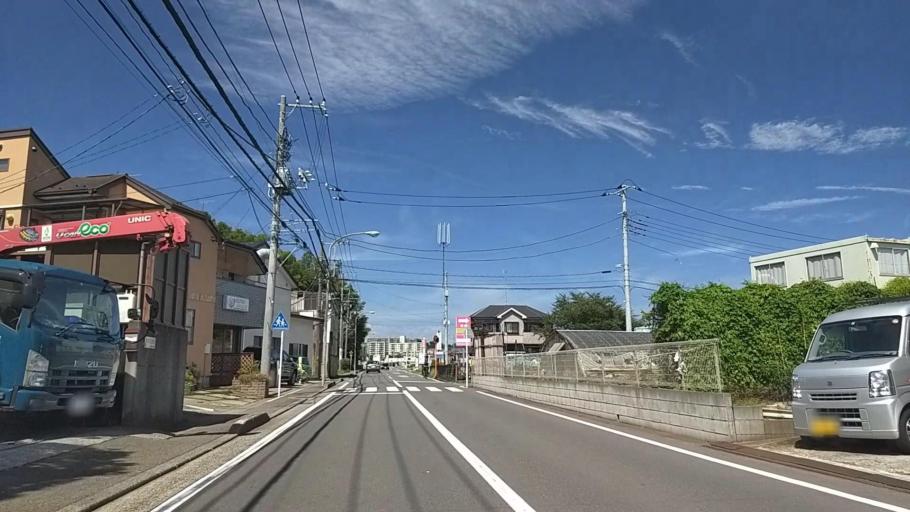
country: JP
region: Tokyo
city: Chofugaoka
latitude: 35.5547
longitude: 139.5672
